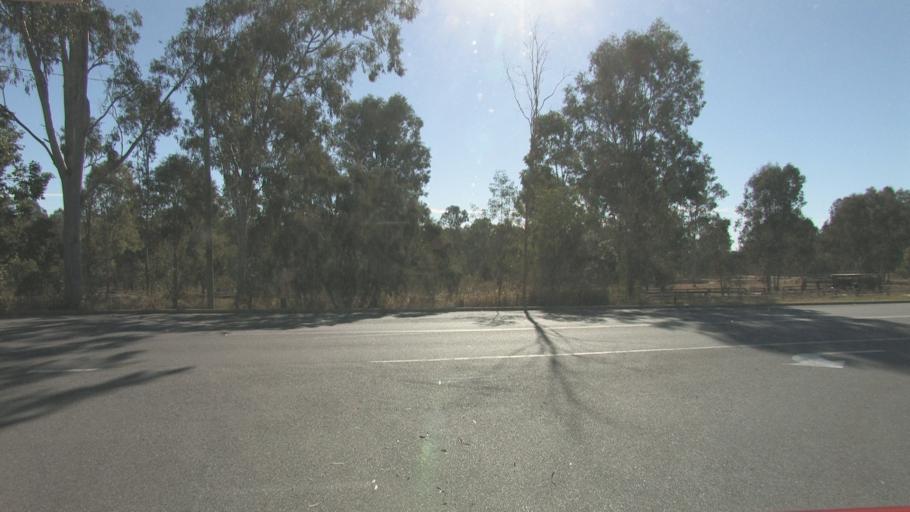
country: AU
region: Queensland
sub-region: Logan
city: North Maclean
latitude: -27.8145
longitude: 152.9888
